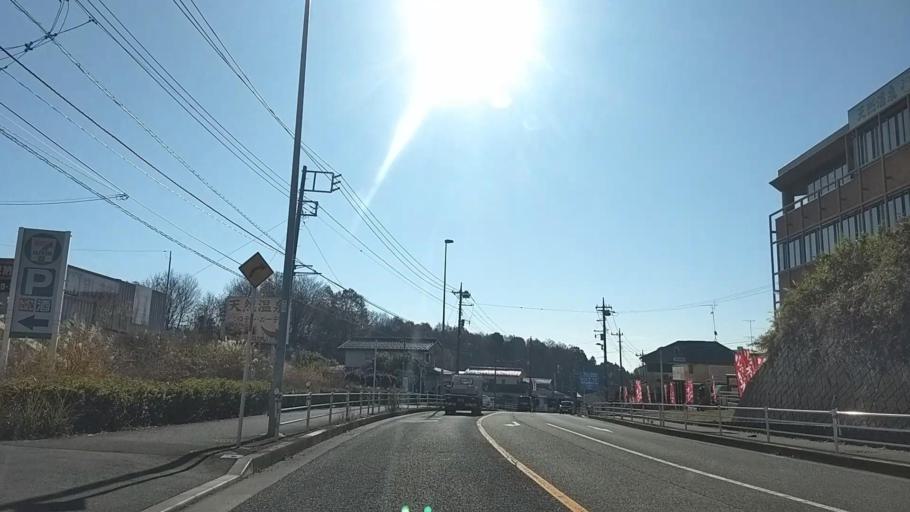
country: JP
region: Tokyo
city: Hachioji
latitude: 35.6098
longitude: 139.3447
